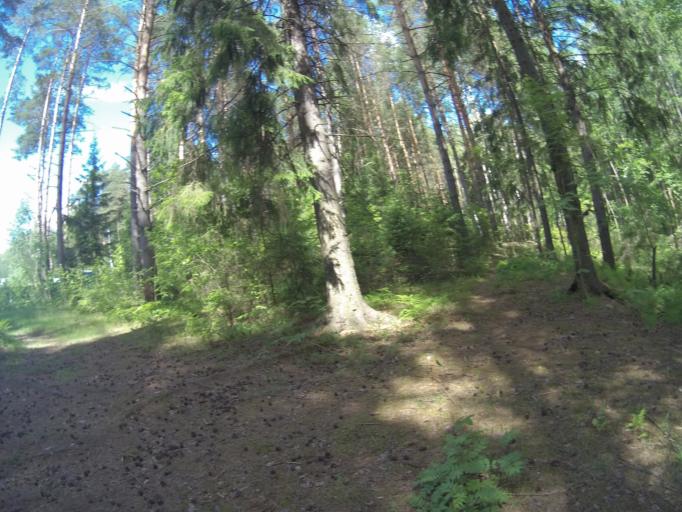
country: RU
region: Vladimir
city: Raduzhnyy
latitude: 56.0070
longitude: 40.2728
